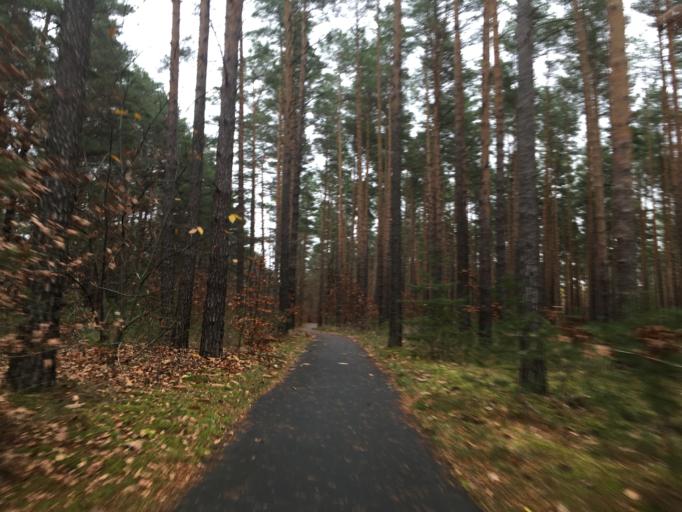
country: DE
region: Brandenburg
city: Mixdorf
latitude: 52.1506
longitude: 14.4277
